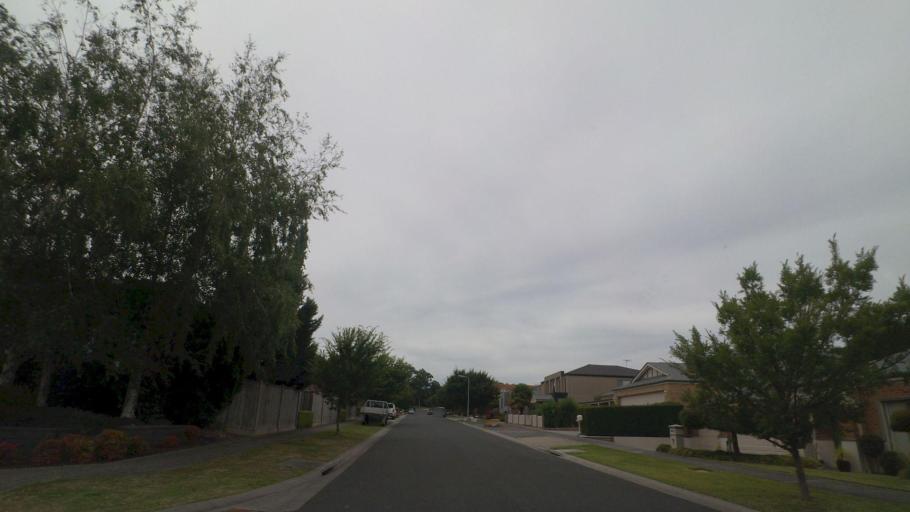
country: AU
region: Victoria
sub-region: Yarra Ranges
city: Kilsyth
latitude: -37.7849
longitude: 145.3422
